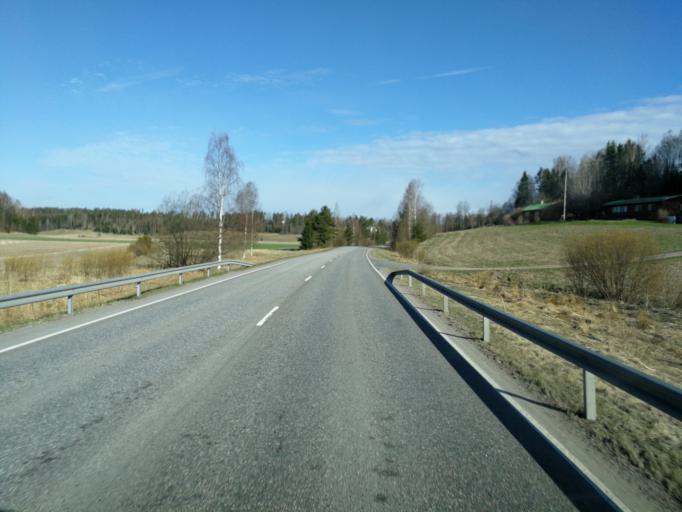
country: FI
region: Uusimaa
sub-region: Helsinki
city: Espoo
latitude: 60.1937
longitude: 24.5643
